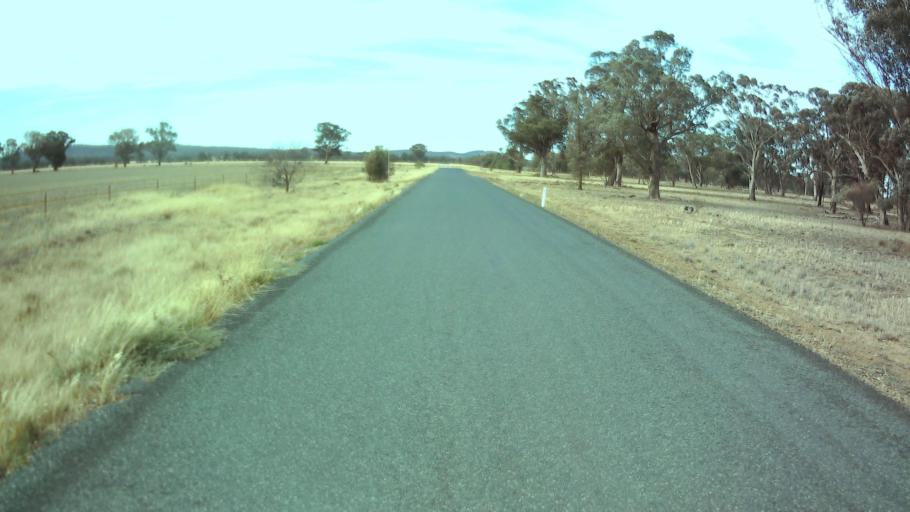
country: AU
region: New South Wales
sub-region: Weddin
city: Grenfell
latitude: -33.8586
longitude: 147.8603
